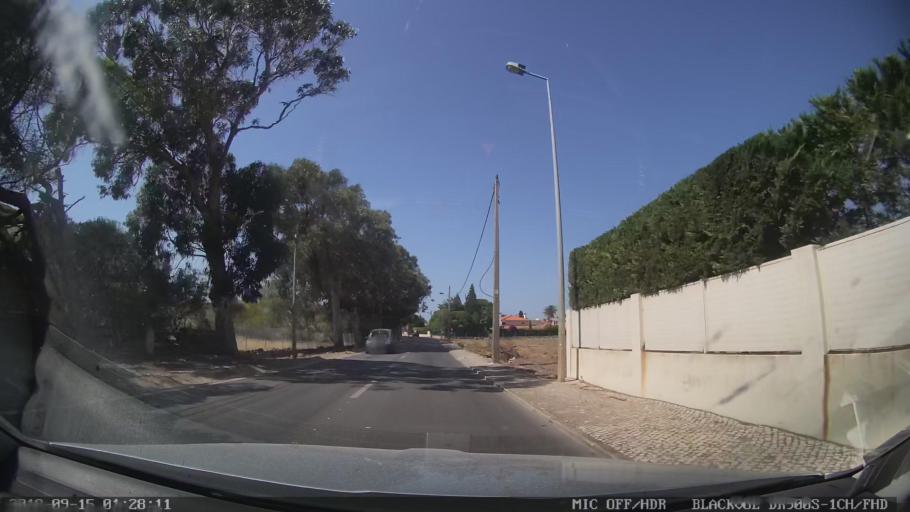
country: PT
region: Lisbon
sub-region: Cascais
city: Cascais
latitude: 38.7169
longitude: -9.4553
